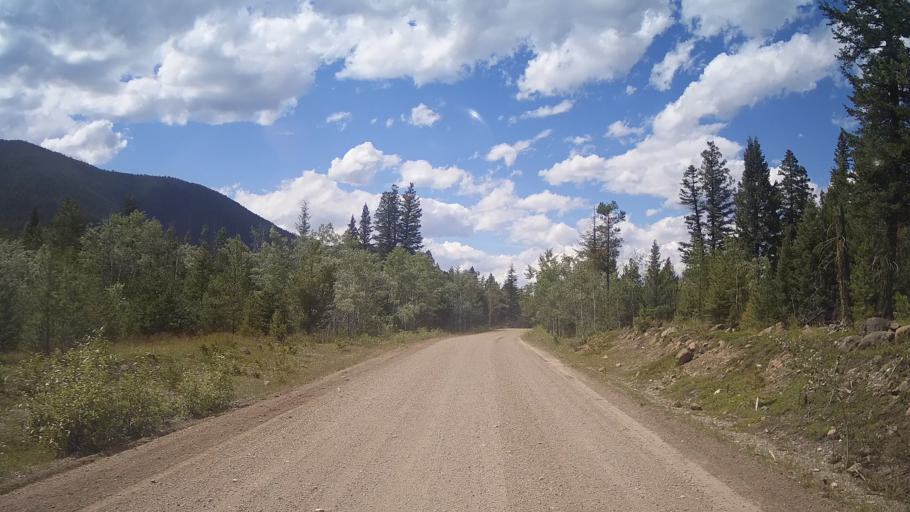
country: CA
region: British Columbia
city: Lillooet
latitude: 51.3256
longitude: -121.8778
